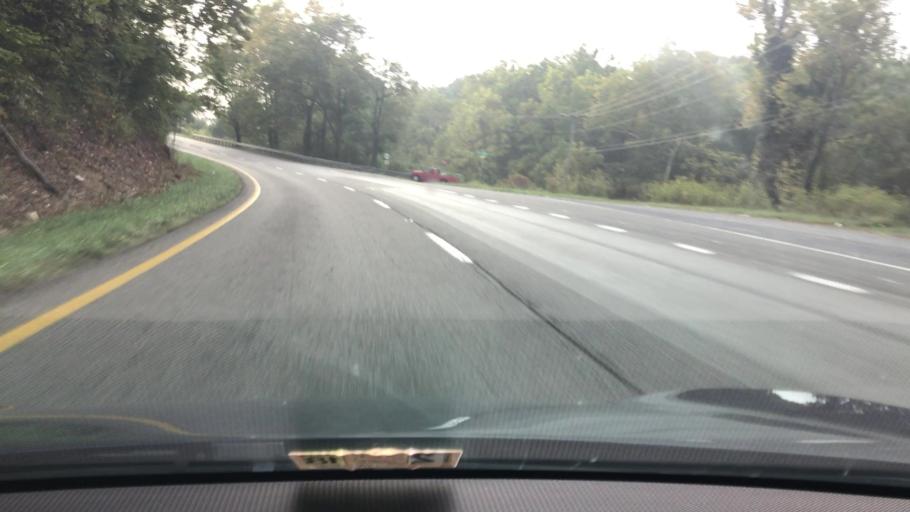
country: US
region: Virginia
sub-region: Botetourt County
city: Blue Ridge
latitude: 37.3885
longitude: -79.7409
